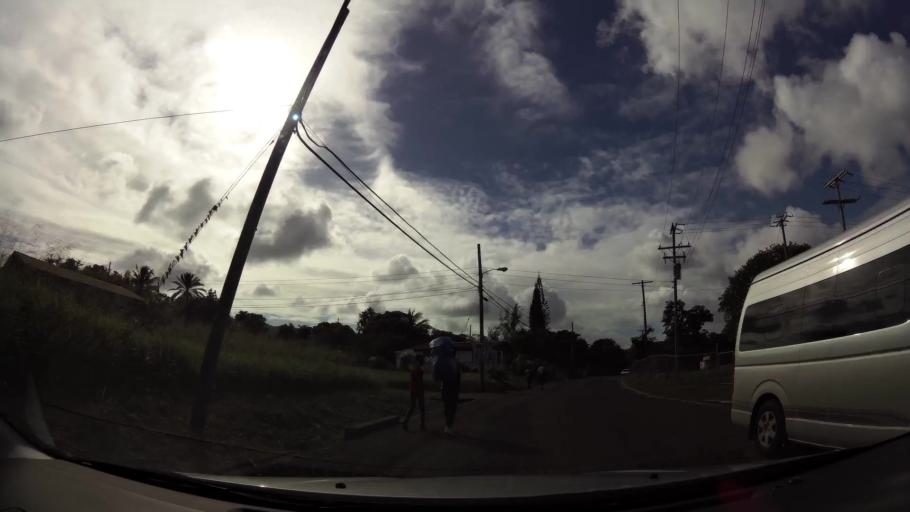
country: AG
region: Saint Peter
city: All Saints
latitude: 17.0505
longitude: -61.7960
